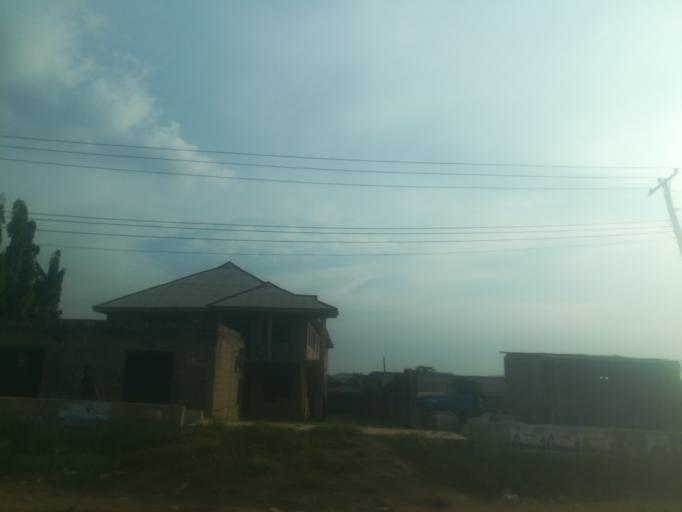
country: NG
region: Ogun
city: Abeokuta
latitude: 7.1674
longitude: 3.3013
